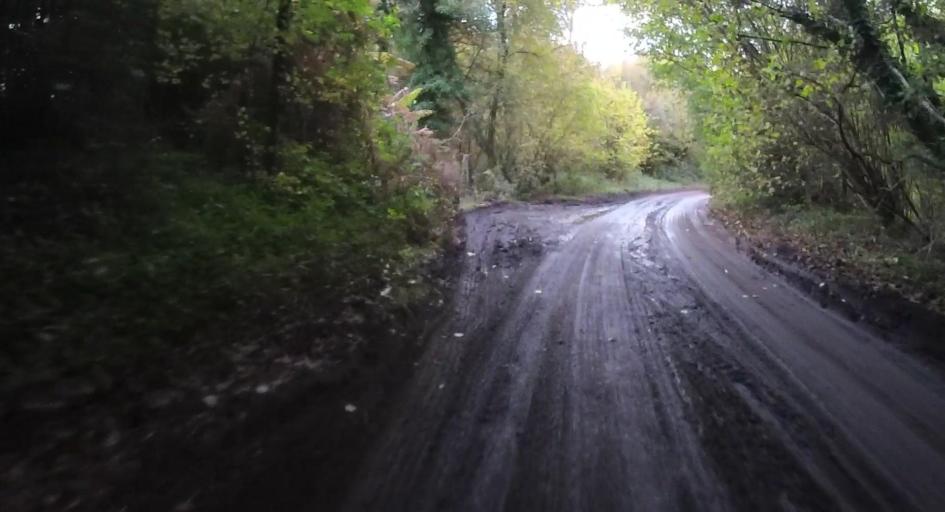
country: GB
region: England
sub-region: Surrey
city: Churt
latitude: 51.1384
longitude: -0.7966
